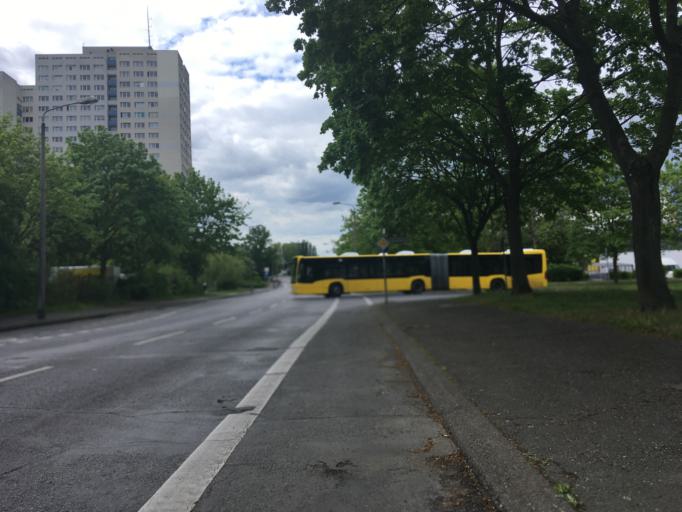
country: DE
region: Berlin
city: Biesdorf
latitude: 52.5344
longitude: 13.5421
